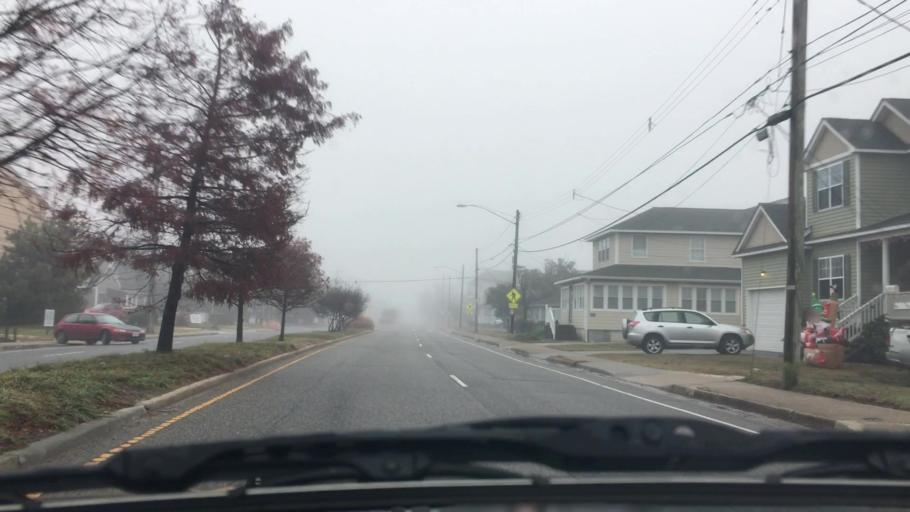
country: US
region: Virginia
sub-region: City of Hampton
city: East Hampton
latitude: 36.9665
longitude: -76.2764
